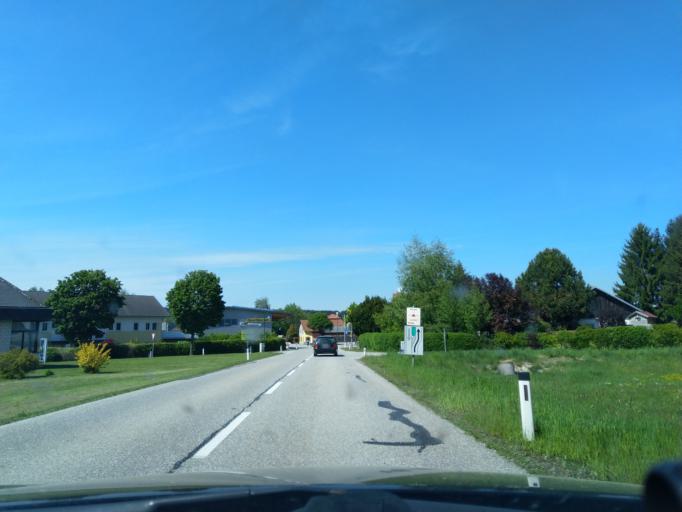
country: AT
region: Upper Austria
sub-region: Politischer Bezirk Ried im Innkreis
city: Ried im Innkreis
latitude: 48.2617
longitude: 13.4191
